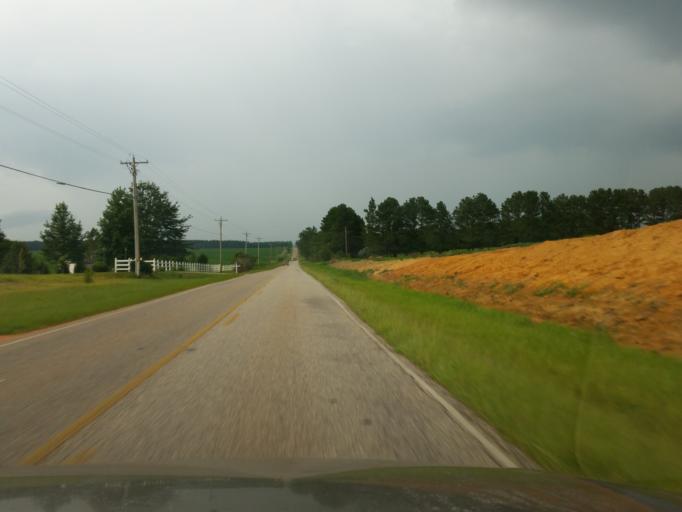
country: US
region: Alabama
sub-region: Baldwin County
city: Robertsdale
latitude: 30.5659
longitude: -87.5816
